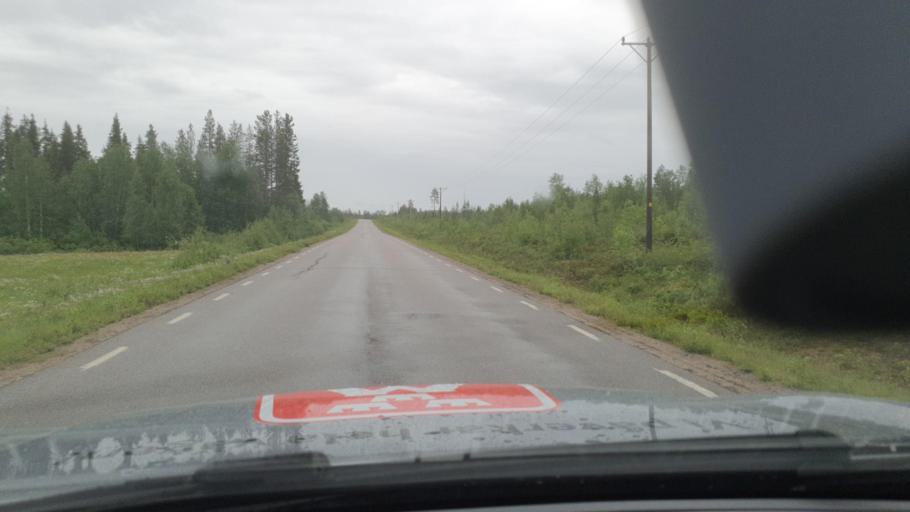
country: SE
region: Norrbotten
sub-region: Pajala Kommun
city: Pajala
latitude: 66.7880
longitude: 23.1278
